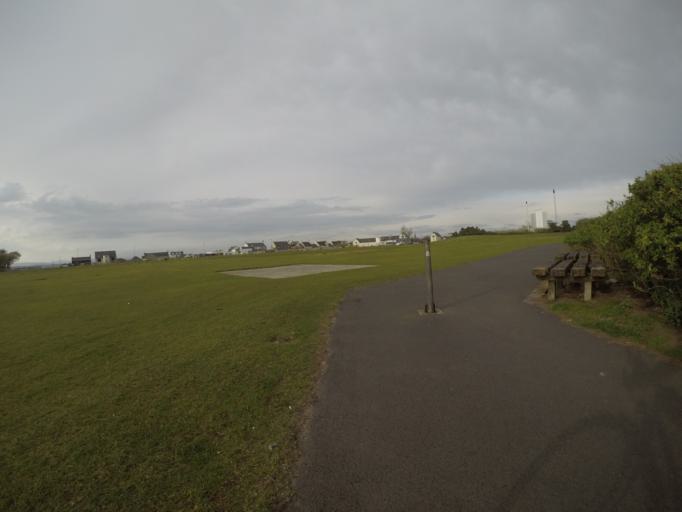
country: GB
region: Scotland
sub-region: North Ayrshire
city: Irvine
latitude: 55.6055
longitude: -4.6858
